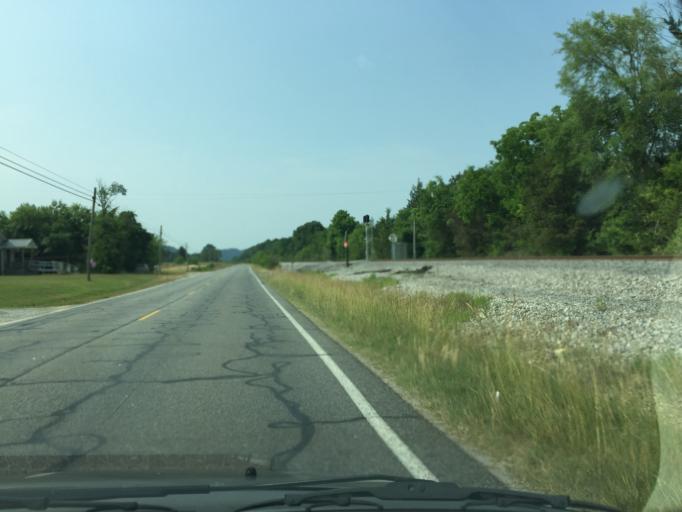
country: US
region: Georgia
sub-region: Catoosa County
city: Ringgold
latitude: 34.9504
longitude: -85.1042
